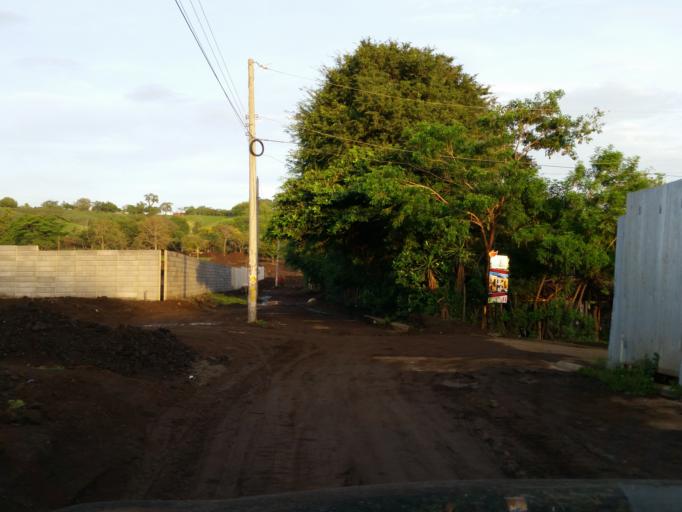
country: NI
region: Masaya
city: Ticuantepe
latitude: 12.0696
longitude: -86.2375
